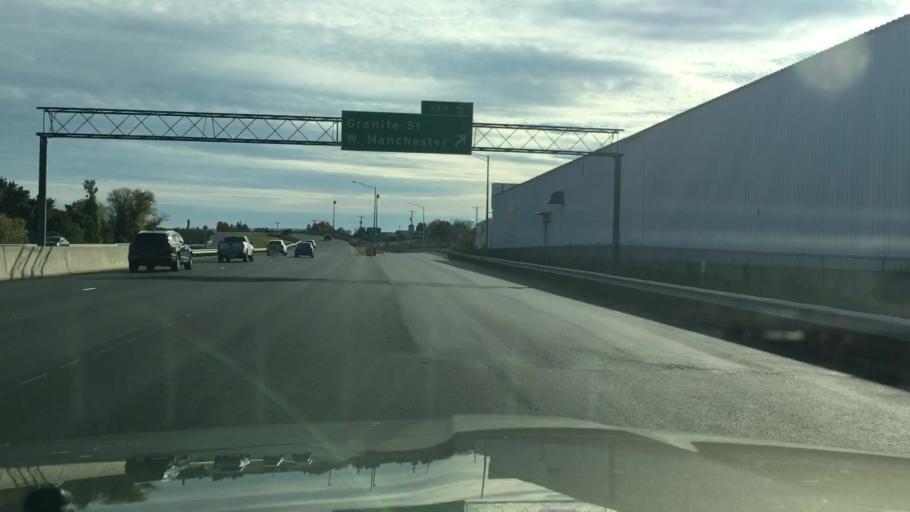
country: US
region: New Hampshire
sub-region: Hillsborough County
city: Manchester
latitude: 42.9894
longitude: -71.4716
